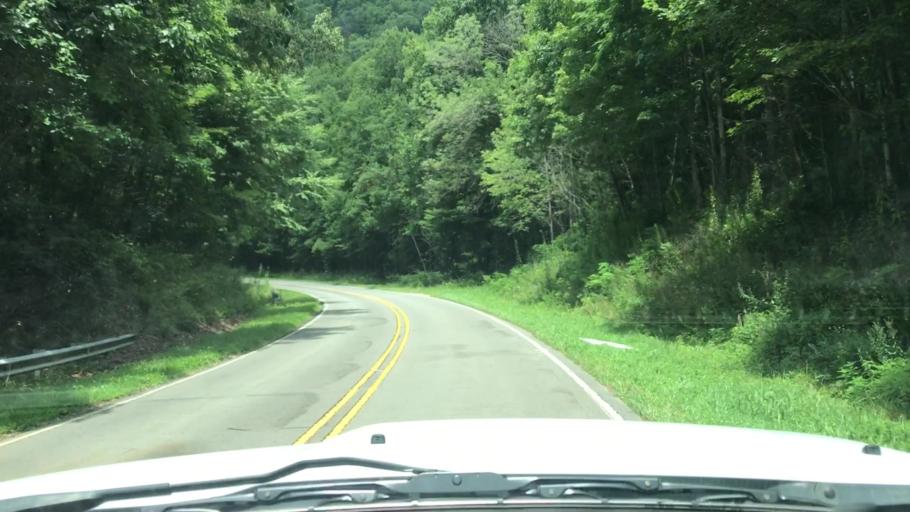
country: US
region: North Carolina
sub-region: Graham County
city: Robbinsville
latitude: 35.3692
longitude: -83.8424
